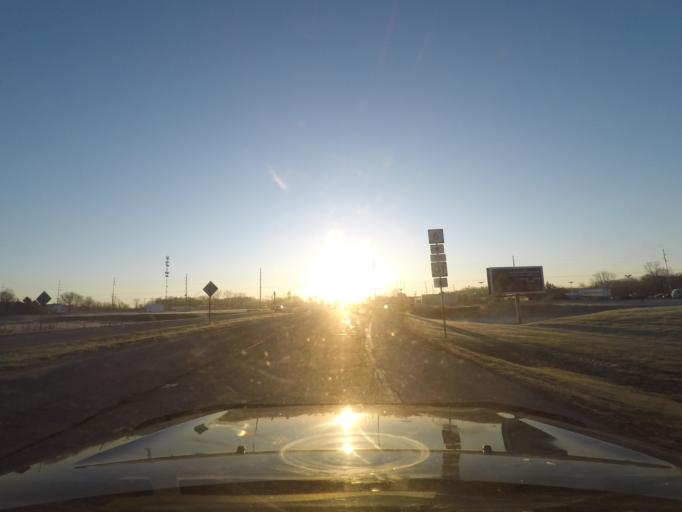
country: US
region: Indiana
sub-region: Marshall County
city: Plymouth
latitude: 41.4494
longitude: -86.3129
